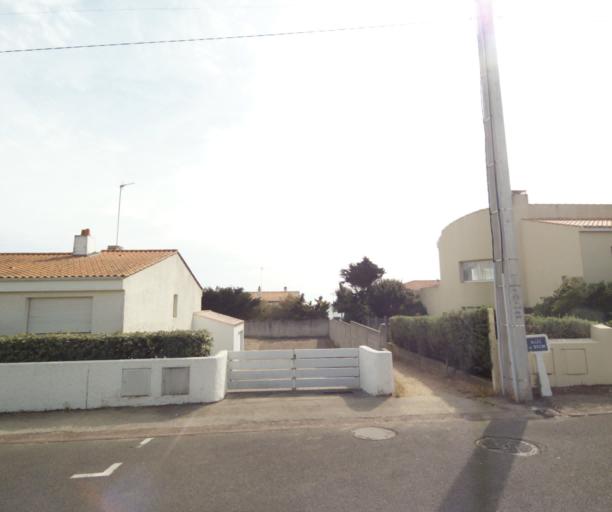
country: FR
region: Pays de la Loire
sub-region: Departement de la Vendee
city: Chateau-d'Olonne
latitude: 46.4780
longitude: -1.7585
